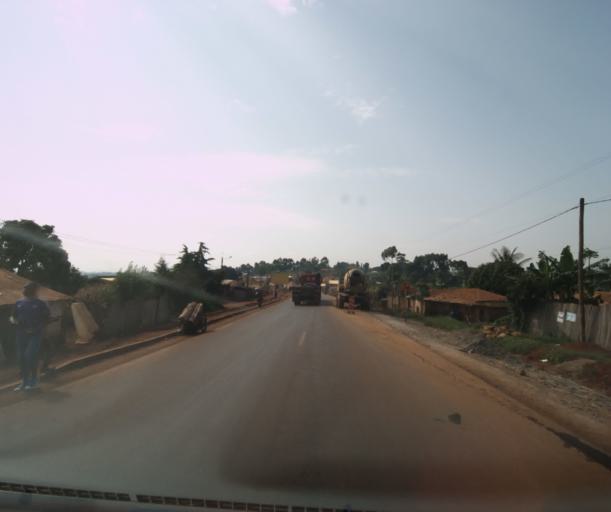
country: CM
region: West
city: Mbouda
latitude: 5.6216
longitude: 10.2667
